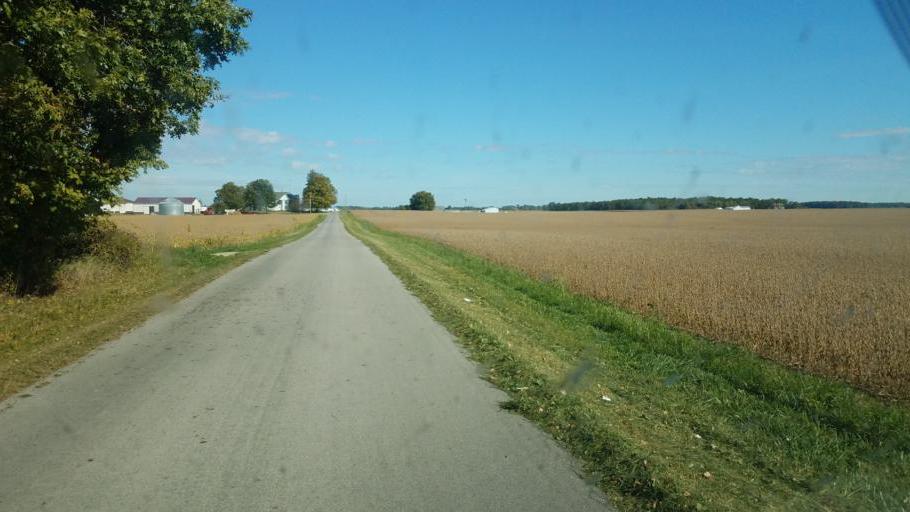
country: US
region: Ohio
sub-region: Wyandot County
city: Upper Sandusky
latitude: 40.7973
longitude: -83.2173
